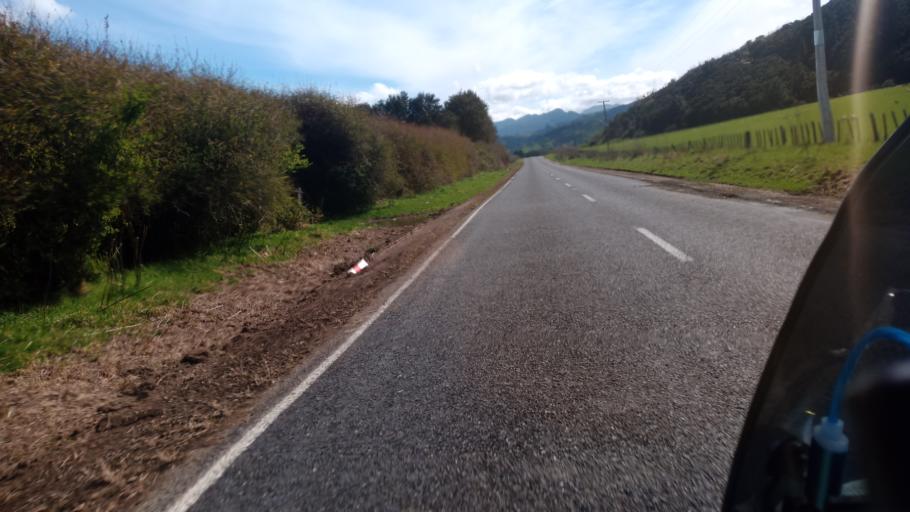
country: NZ
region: Gisborne
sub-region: Gisborne District
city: Gisborne
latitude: -37.8751
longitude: 178.2830
